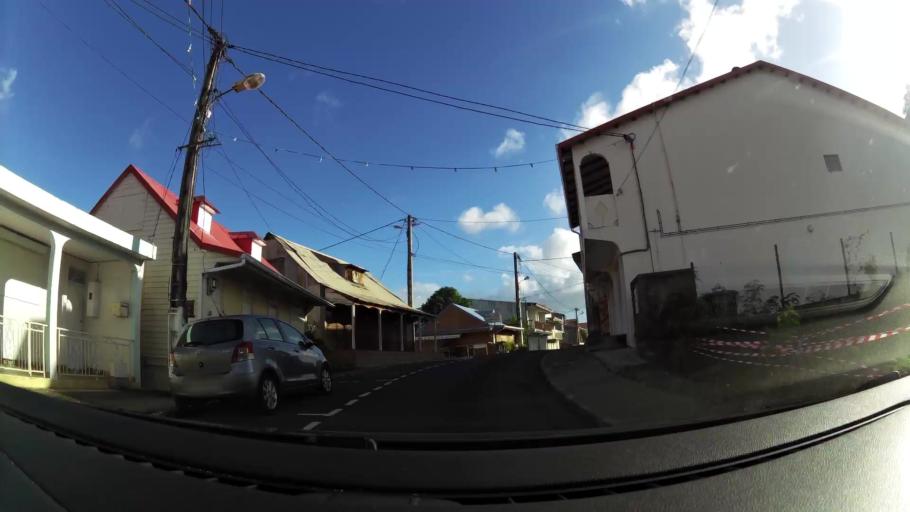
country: GP
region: Guadeloupe
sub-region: Guadeloupe
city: Pointe-Noire
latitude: 16.2348
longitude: -61.7902
